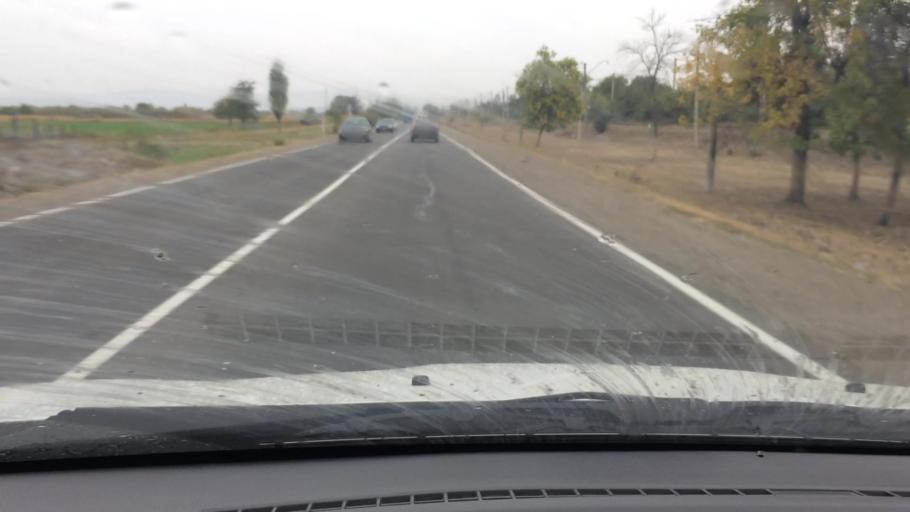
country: GE
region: Kvemo Kartli
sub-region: Marneuli
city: Marneuli
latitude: 41.4233
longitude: 44.8240
